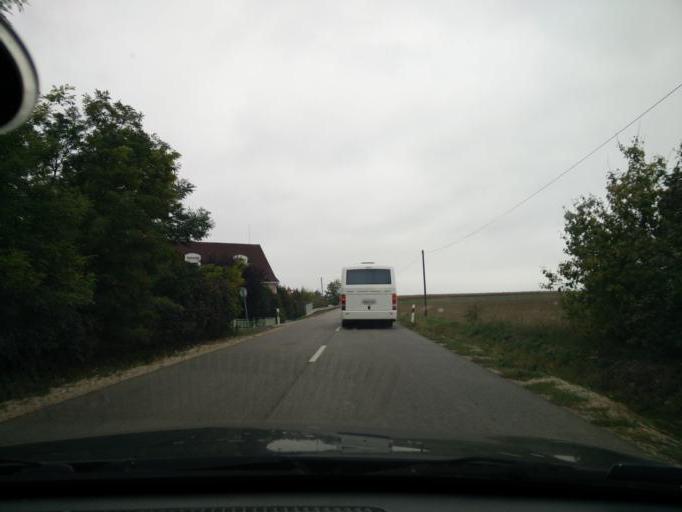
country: HU
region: Komarom-Esztergom
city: Bajna
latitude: 47.6832
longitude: 18.6114
